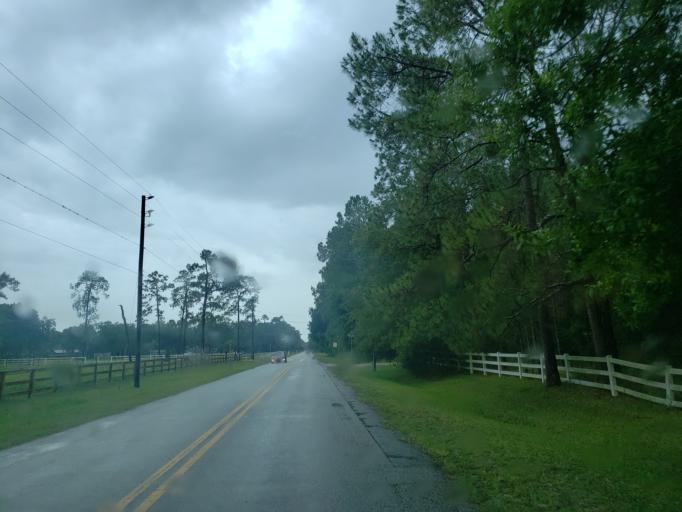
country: US
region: Florida
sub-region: Pasco County
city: Wesley Chapel
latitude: 28.2735
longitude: -82.3530
